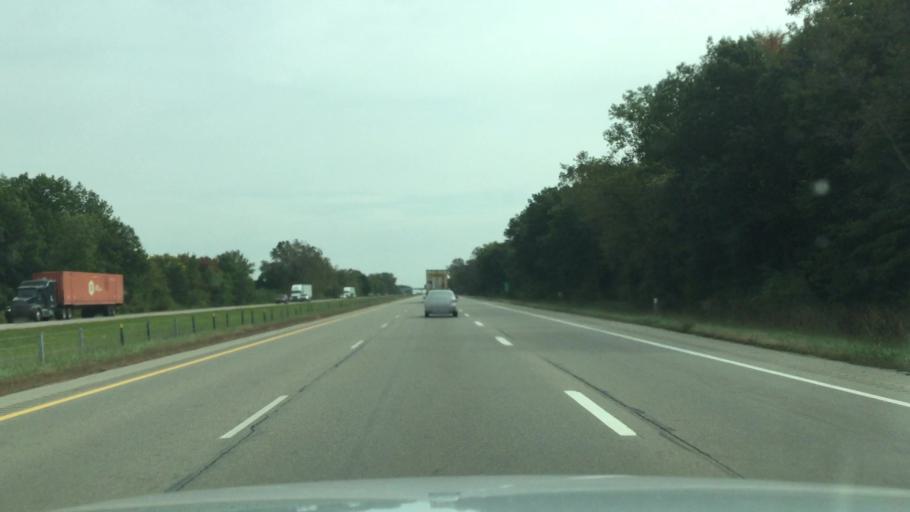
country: US
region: Michigan
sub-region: Shiawassee County
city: Durand
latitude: 42.9642
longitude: -83.9244
